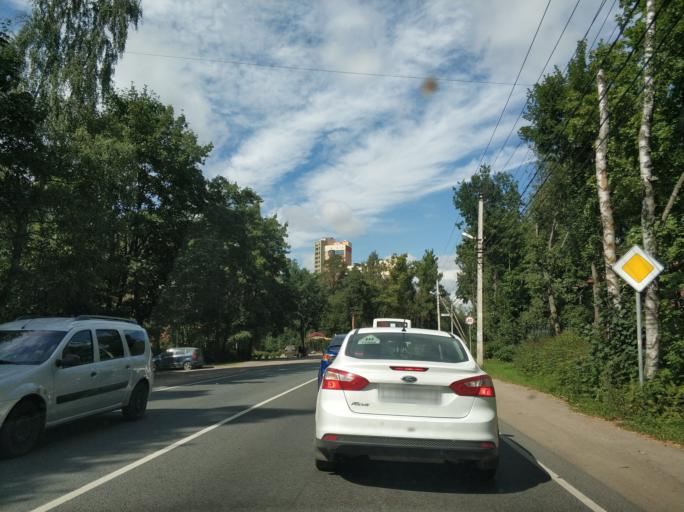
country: RU
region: Leningrad
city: Vsevolozhsk
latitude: 60.0299
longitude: 30.6392
